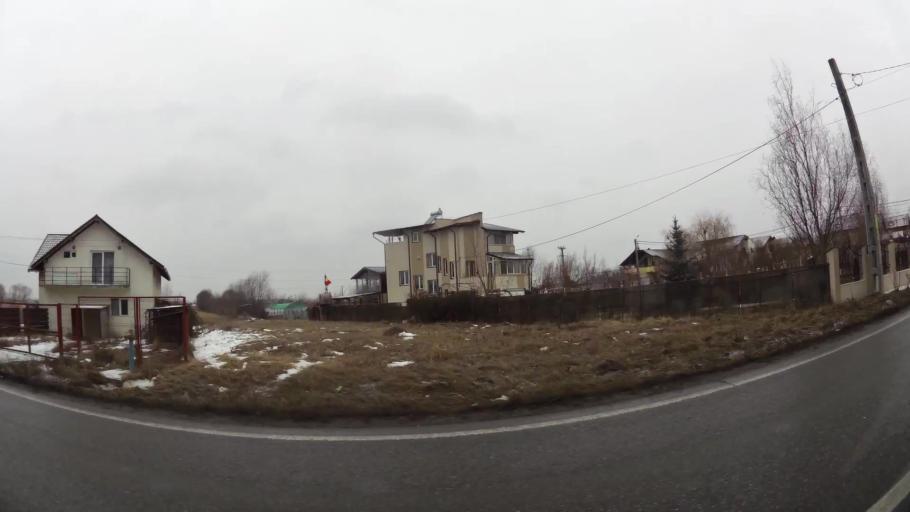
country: RO
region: Dambovita
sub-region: Comuna Aninoasa
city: Viforata
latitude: 44.9491
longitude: 25.4813
